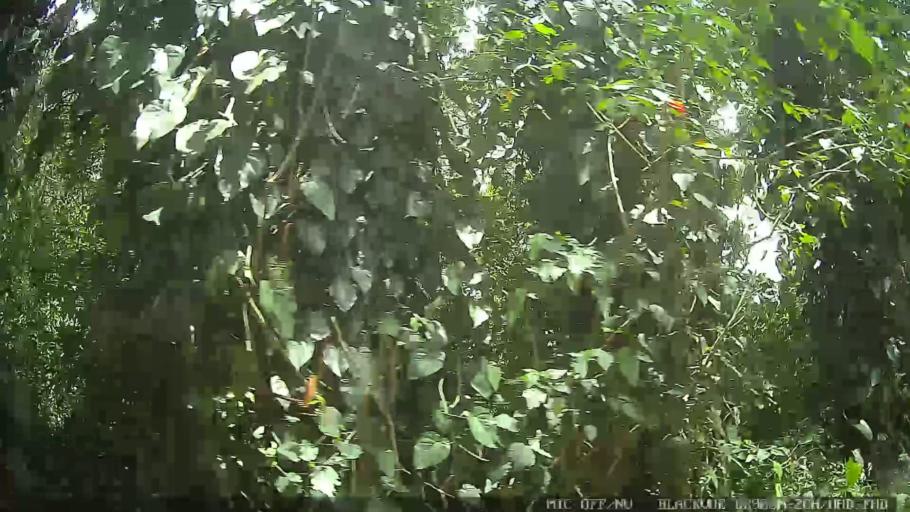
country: BR
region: Sao Paulo
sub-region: Mogi das Cruzes
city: Mogi das Cruzes
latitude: -23.4983
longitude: -46.2030
